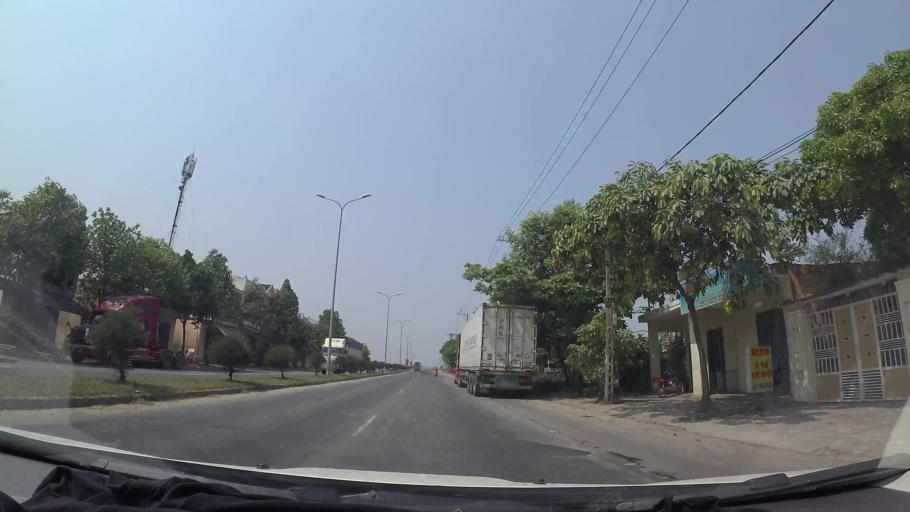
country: VN
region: Da Nang
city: Cam Le
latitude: 15.9969
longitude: 108.1918
